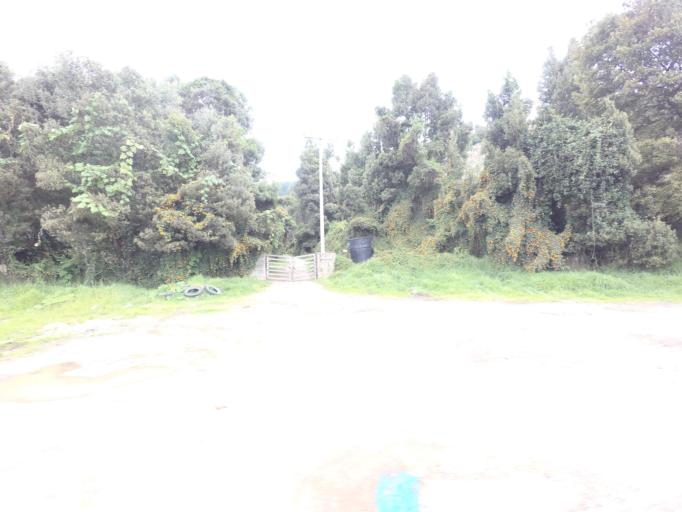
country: CO
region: Cundinamarca
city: Cajica
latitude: 4.9434
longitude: -74.0291
